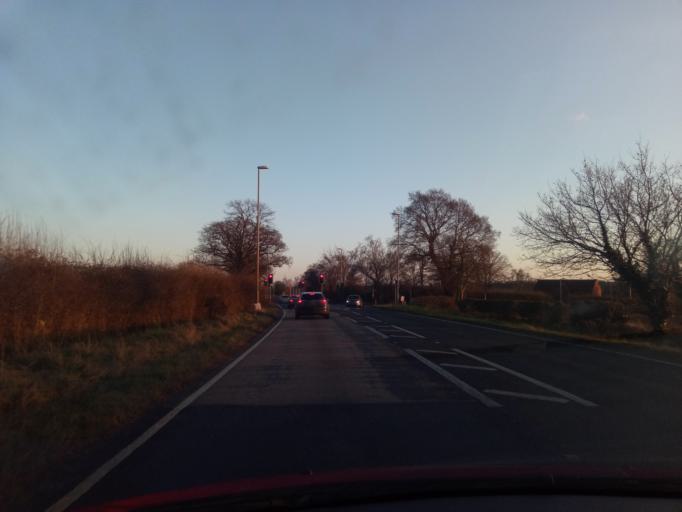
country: GB
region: England
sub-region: Nottinghamshire
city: Burton Joyce
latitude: 53.0357
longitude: -1.0488
